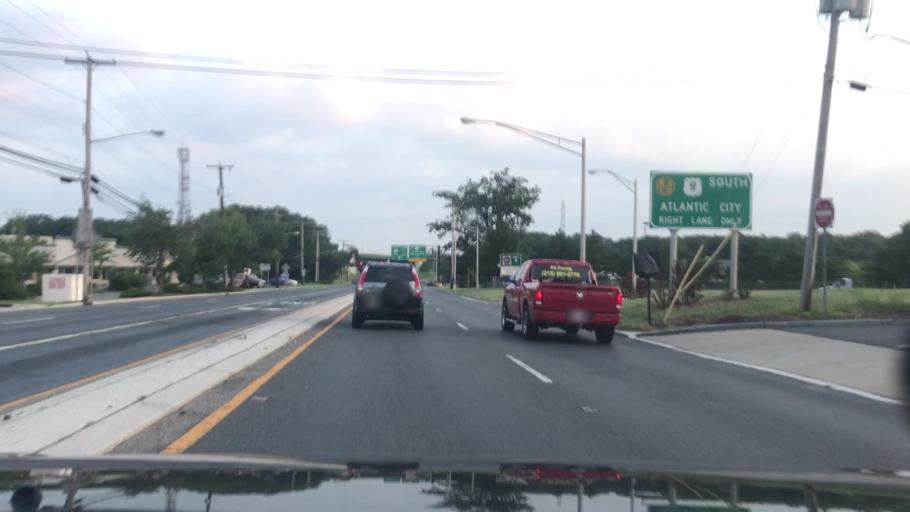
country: US
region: New Jersey
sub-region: Ocean County
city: Silver Ridge
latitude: 39.9925
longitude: -74.2114
